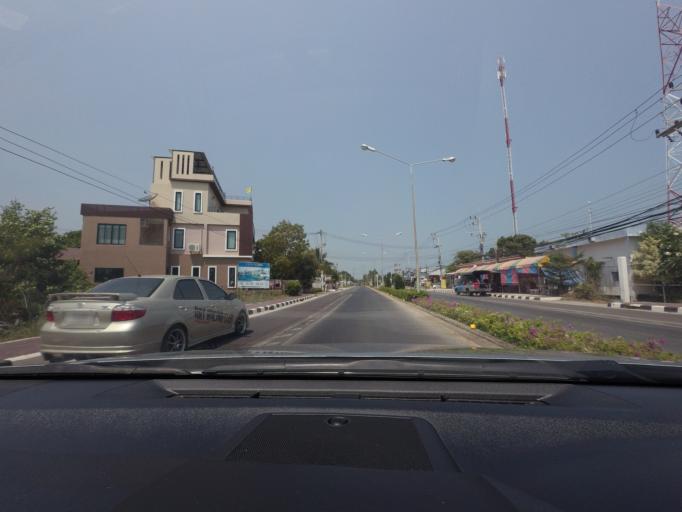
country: TH
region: Phetchaburi
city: Cha-am
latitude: 12.8168
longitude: 99.9817
